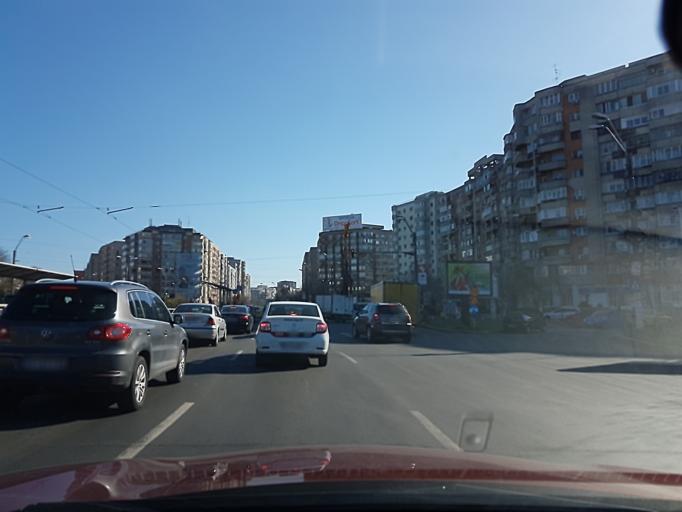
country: RO
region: Bucuresti
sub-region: Municipiul Bucuresti
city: Bucharest
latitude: 44.4253
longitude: 26.1374
